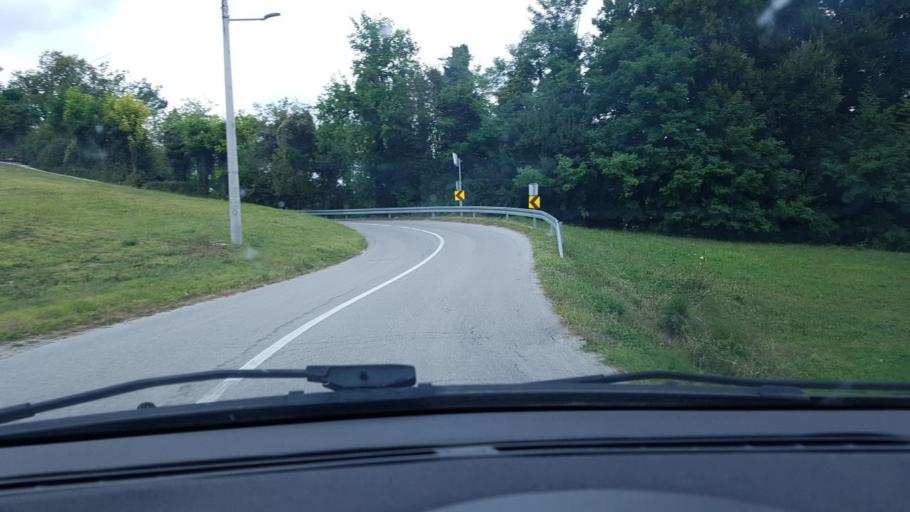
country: SI
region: Podcetrtek
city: Podcetrtek
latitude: 46.1491
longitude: 15.6609
